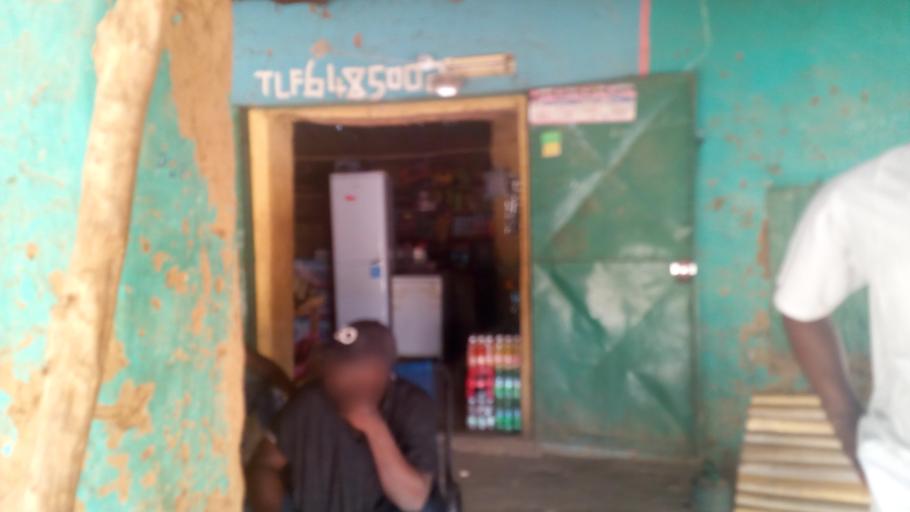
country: ML
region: Kayes
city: Yelimane
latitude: 14.6418
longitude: -10.6985
